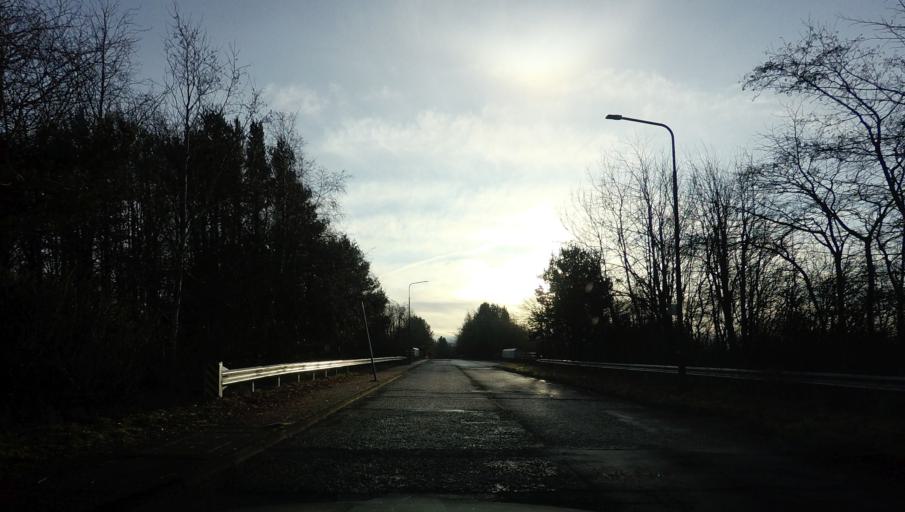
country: GB
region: Scotland
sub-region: West Lothian
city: Mid Calder
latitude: 55.8752
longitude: -3.4860
